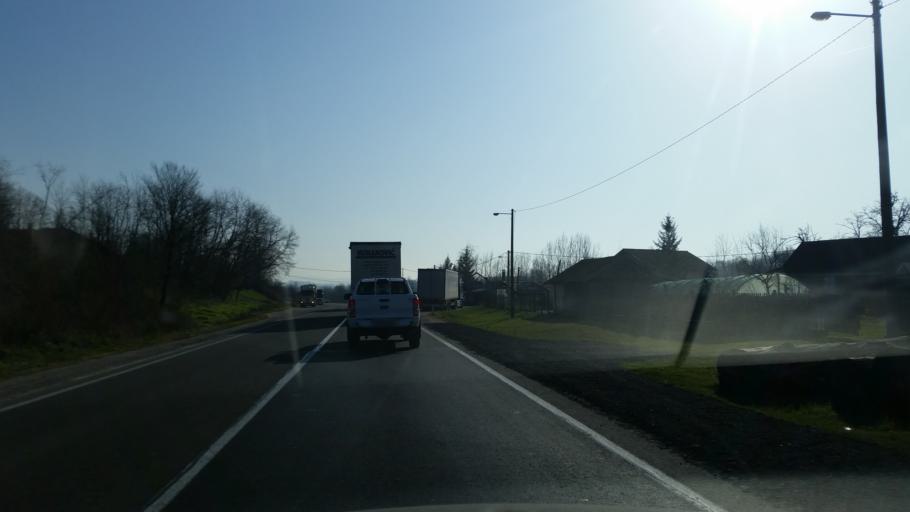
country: RS
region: Central Serbia
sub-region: Belgrade
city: Lazarevac
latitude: 44.3207
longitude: 20.2270
